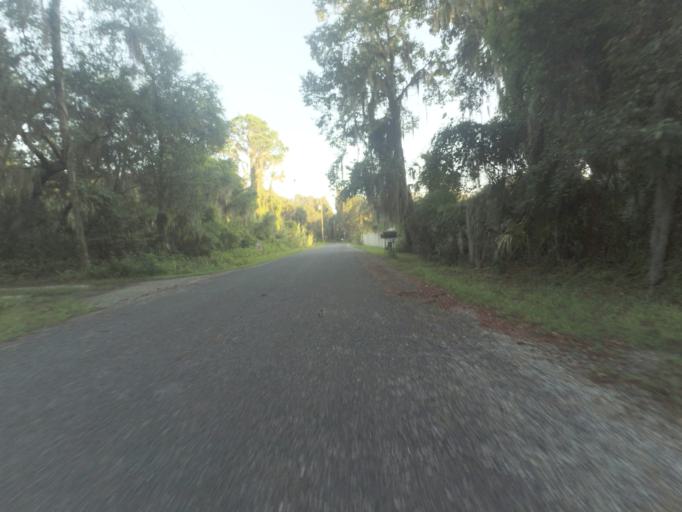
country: US
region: Florida
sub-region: Lake County
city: Astor
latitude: 29.2853
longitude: -81.6486
